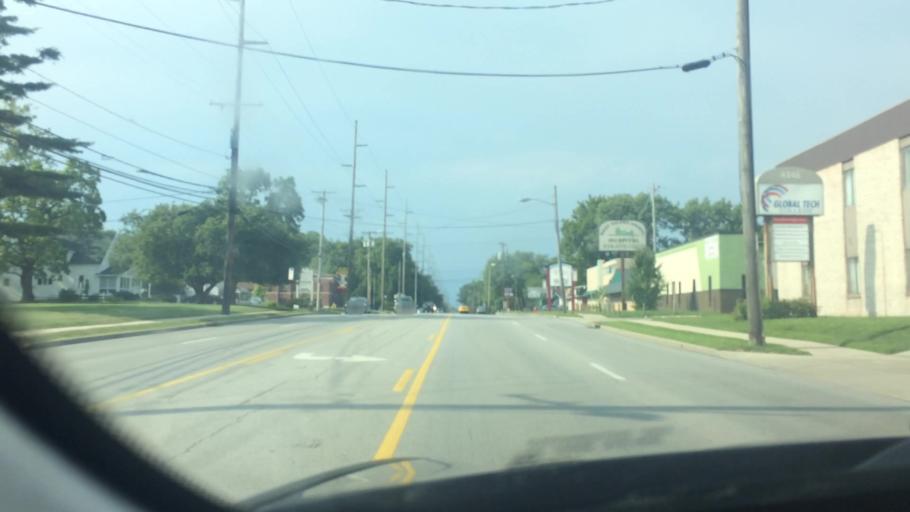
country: US
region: Ohio
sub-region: Lucas County
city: Ottawa Hills
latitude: 41.6971
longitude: -83.6234
